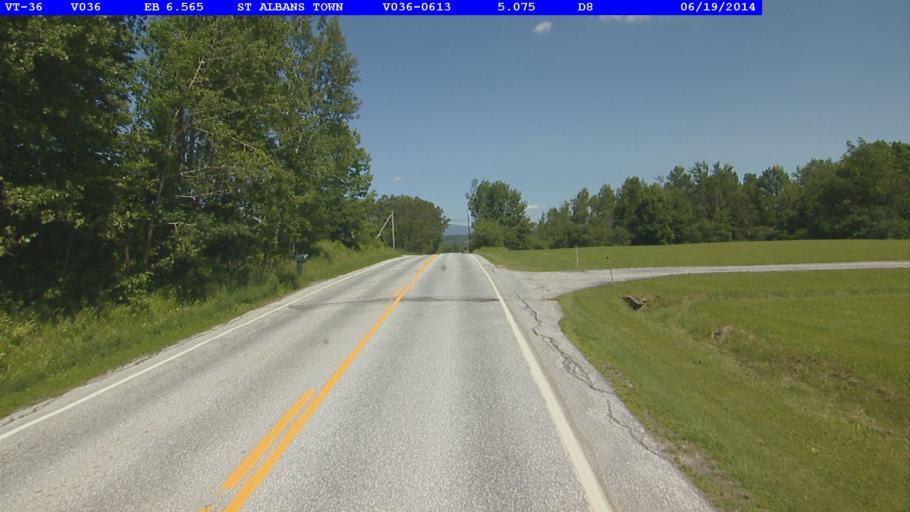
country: US
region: Vermont
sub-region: Franklin County
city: Saint Albans
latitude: 44.7900
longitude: -73.0347
